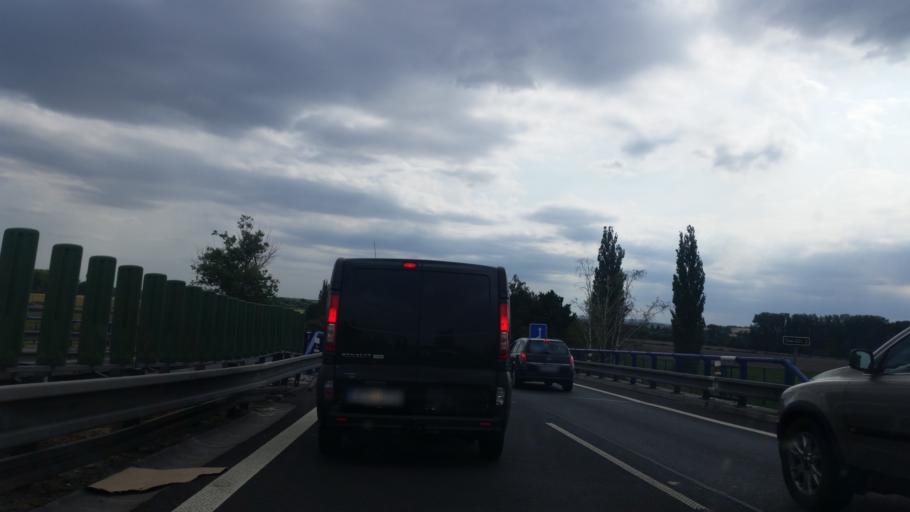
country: CZ
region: Olomoucky
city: Hnevotin
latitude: 49.5466
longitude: 17.1783
